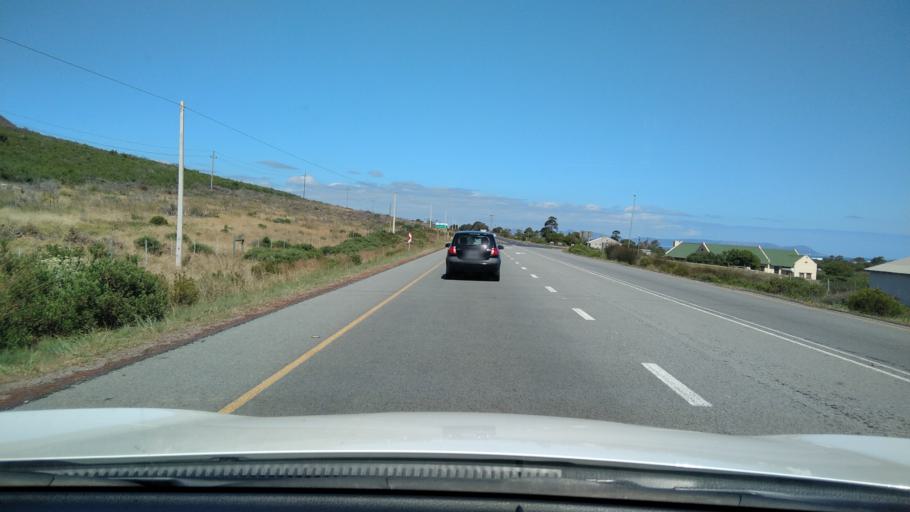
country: ZA
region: Western Cape
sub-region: Overberg District Municipality
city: Hermanus
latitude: -34.4050
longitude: 19.1473
